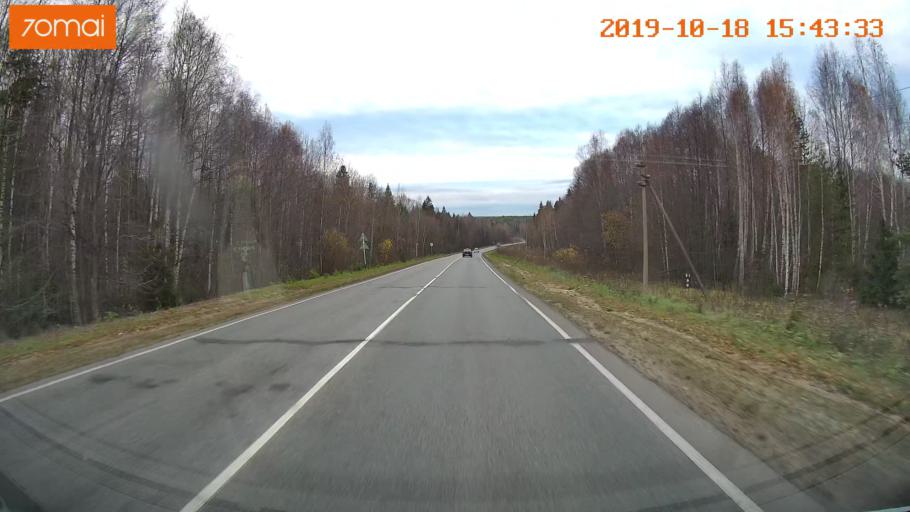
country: RU
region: Vladimir
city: Golovino
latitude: 55.9691
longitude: 40.5498
